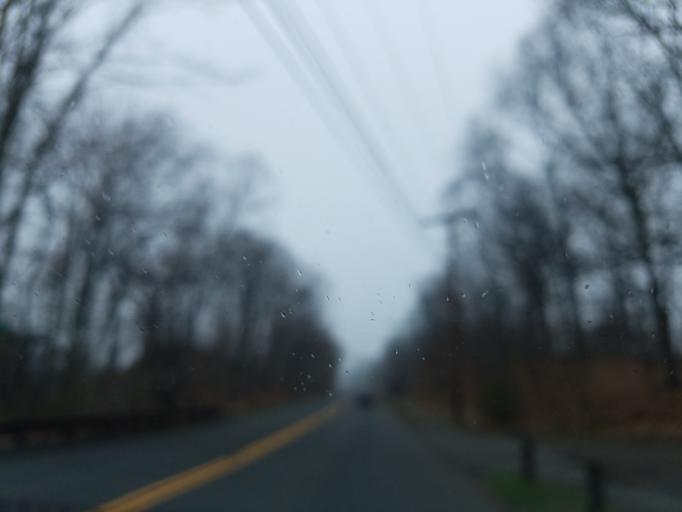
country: US
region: Connecticut
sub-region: Fairfield County
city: Darien
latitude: 41.0718
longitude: -73.4821
